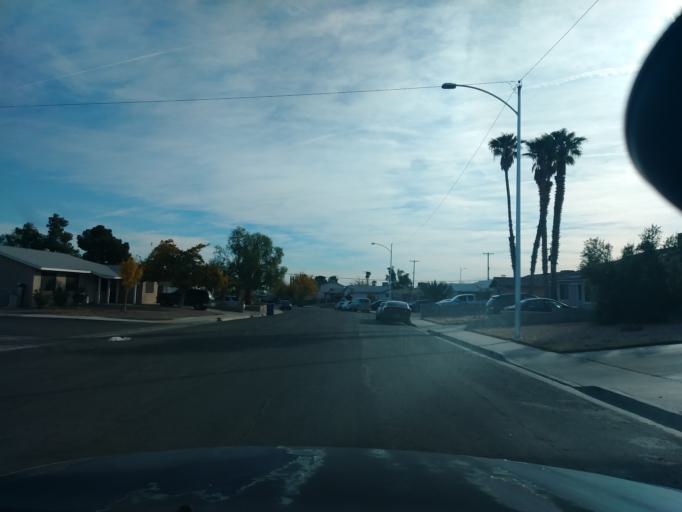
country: US
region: Nevada
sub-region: Clark County
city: Spring Valley
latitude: 36.1631
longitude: -115.2377
